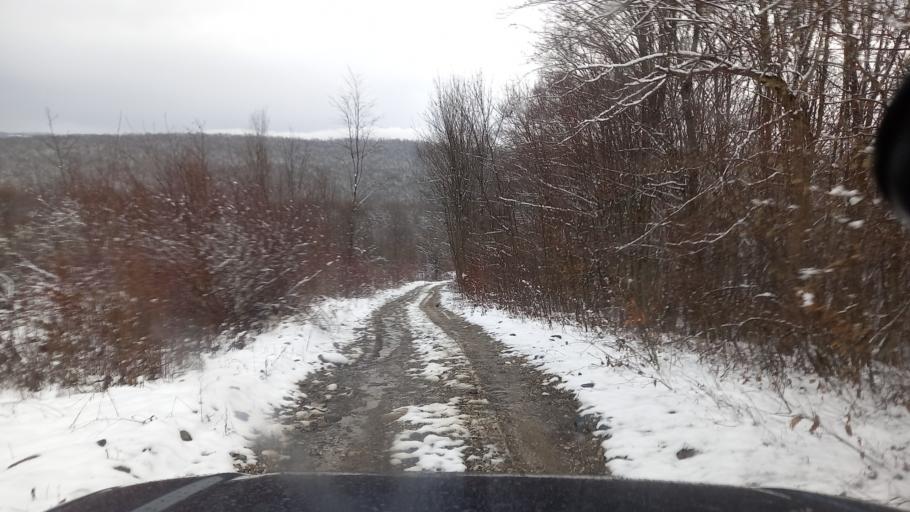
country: RU
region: Adygeya
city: Abadzekhskaya
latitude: 44.3704
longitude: 40.2579
